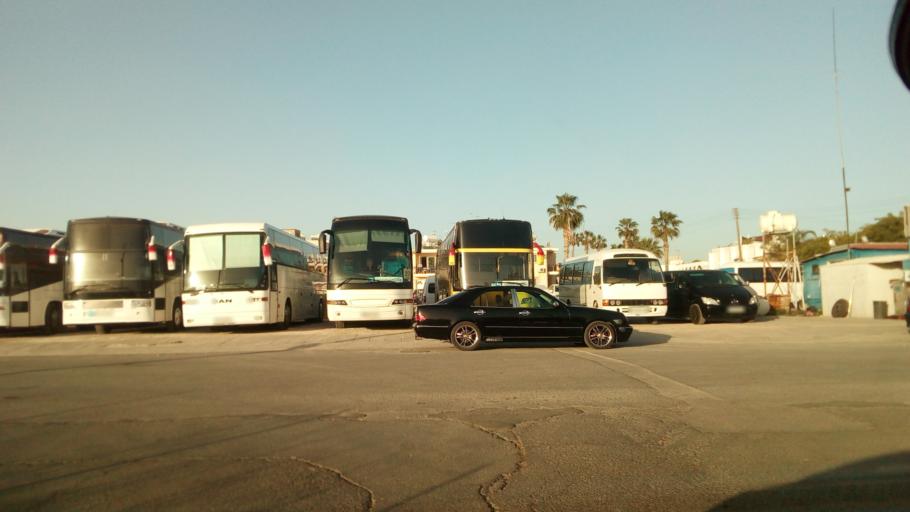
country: CY
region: Larnaka
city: Voroklini
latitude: 34.9705
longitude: 33.6687
